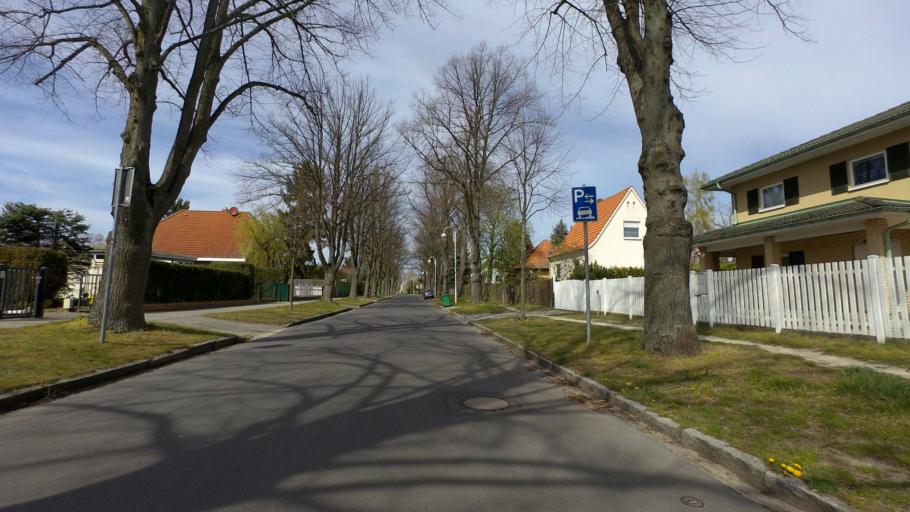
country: DE
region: Berlin
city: Lichtenrade
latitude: 52.3458
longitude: 13.4146
